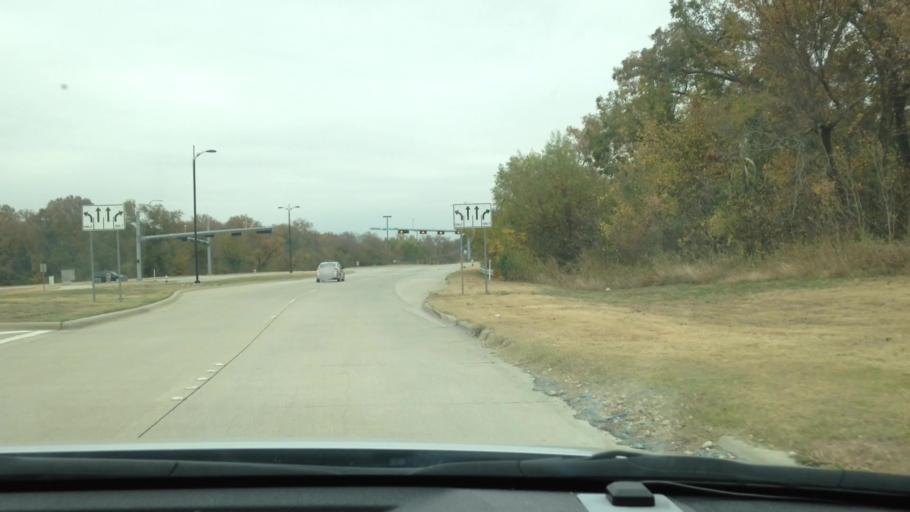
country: US
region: Texas
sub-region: Collin County
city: Allen
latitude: 33.1246
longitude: -96.7194
